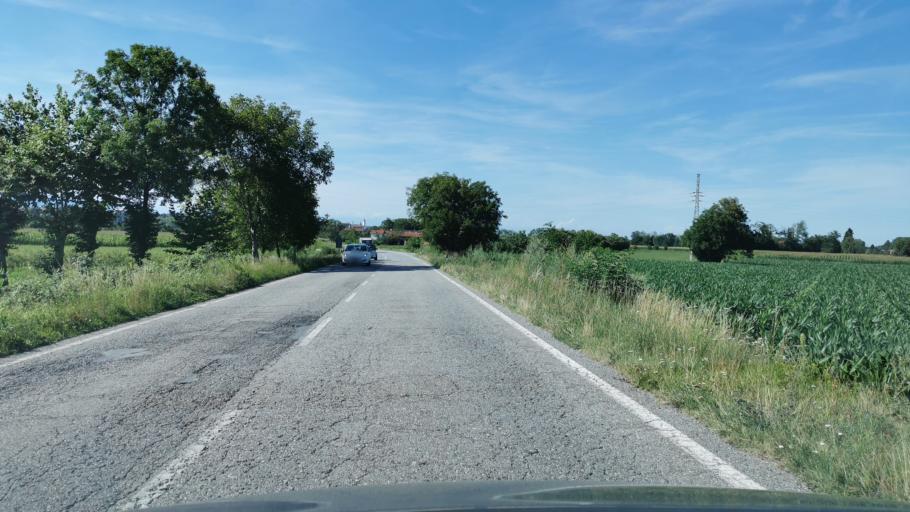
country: IT
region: Piedmont
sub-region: Provincia di Cuneo
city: Cuneo
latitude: 44.3691
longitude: 7.5603
